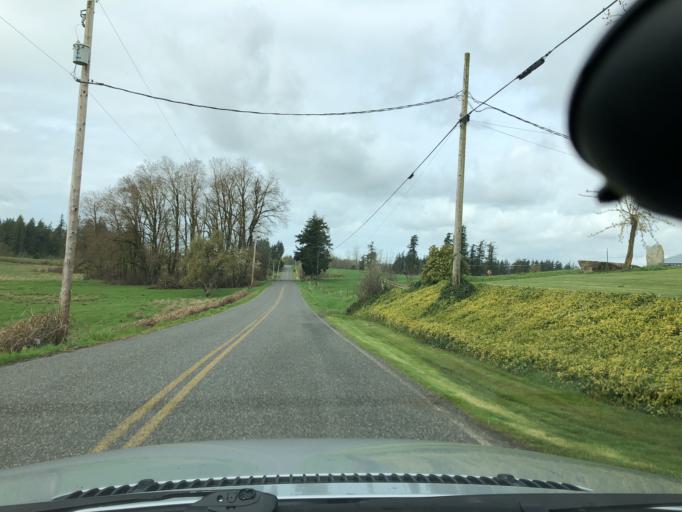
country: CA
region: British Columbia
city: Langley
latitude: 48.9795
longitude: -122.5643
